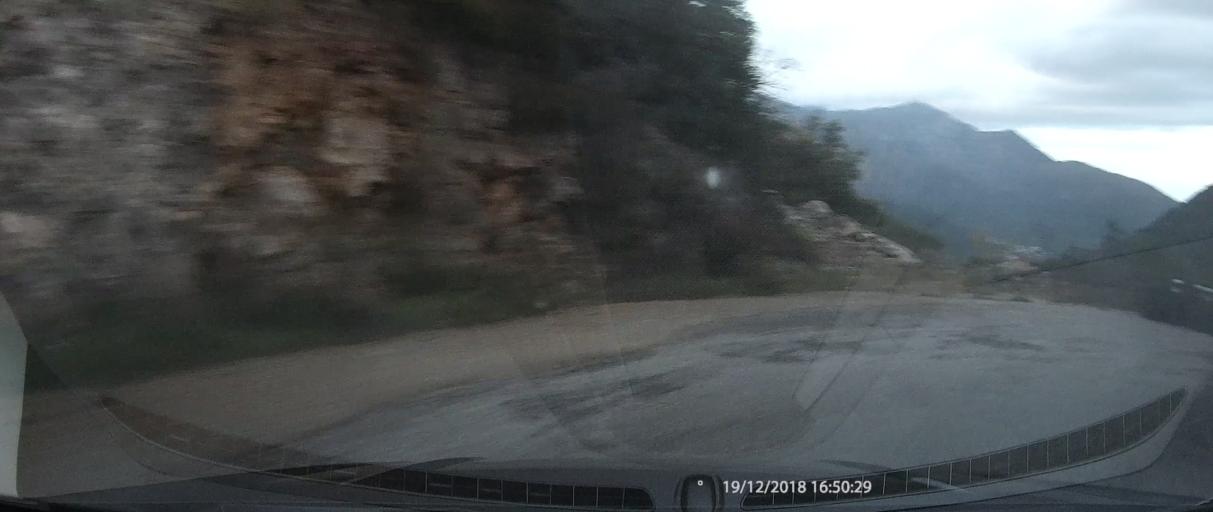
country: GR
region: Peloponnese
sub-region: Nomos Lakonias
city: Sykea
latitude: 36.9522
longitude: 22.9933
